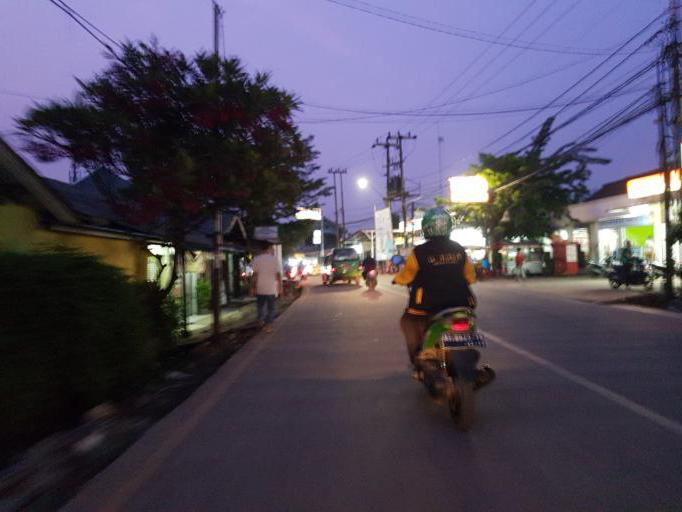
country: ID
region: West Java
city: Serpong
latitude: -6.3178
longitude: 106.6637
